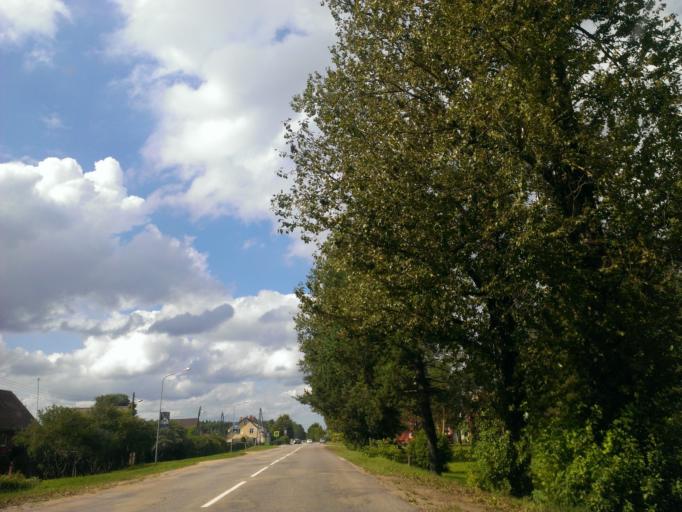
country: LV
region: Garkalne
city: Garkalne
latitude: 56.9684
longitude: 24.4846
